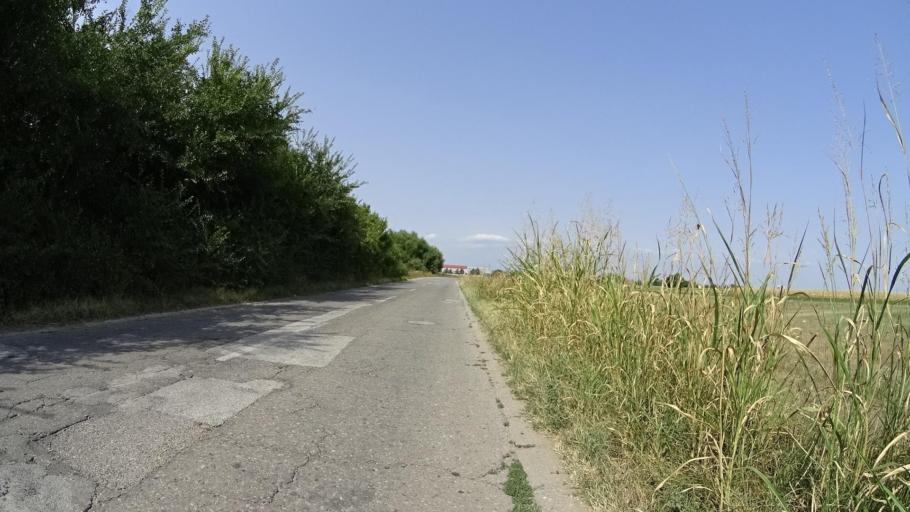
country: BG
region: Plovdiv
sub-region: Obshtina Plovdiv
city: Plovdiv
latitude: 42.2339
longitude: 24.7866
